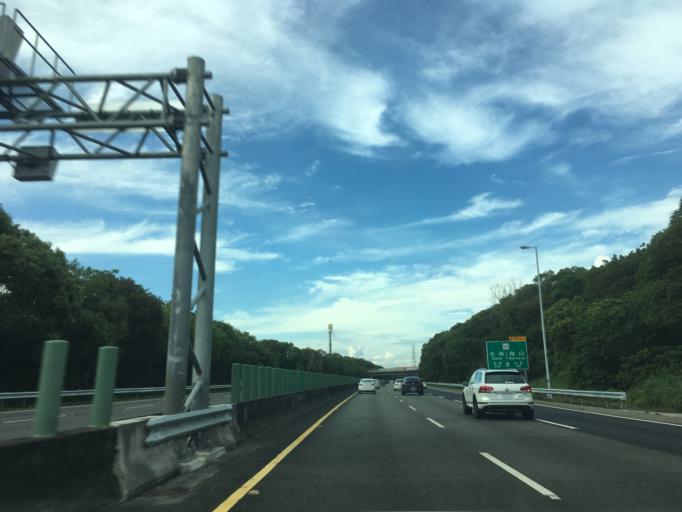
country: TW
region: Taiwan
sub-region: Chiayi
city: Jiayi Shi
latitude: 23.5783
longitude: 120.5088
